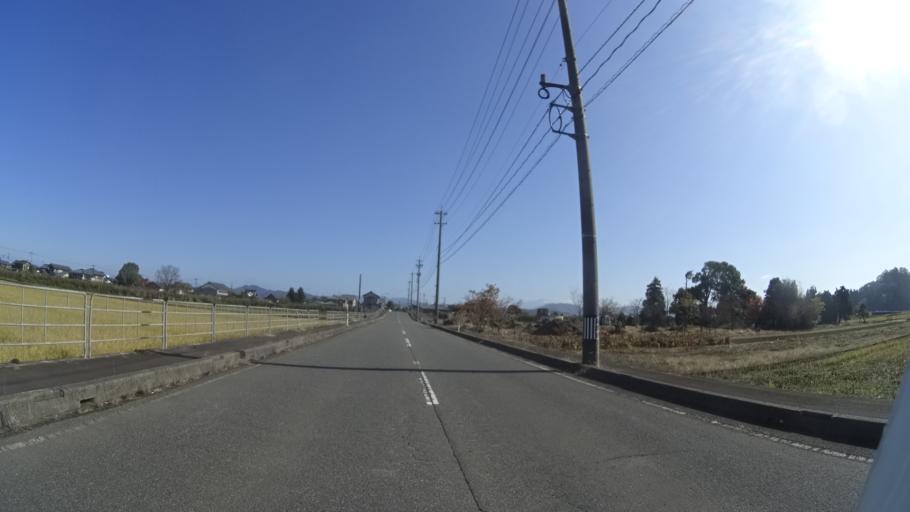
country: JP
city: Asahi
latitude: 35.9633
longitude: 136.1403
